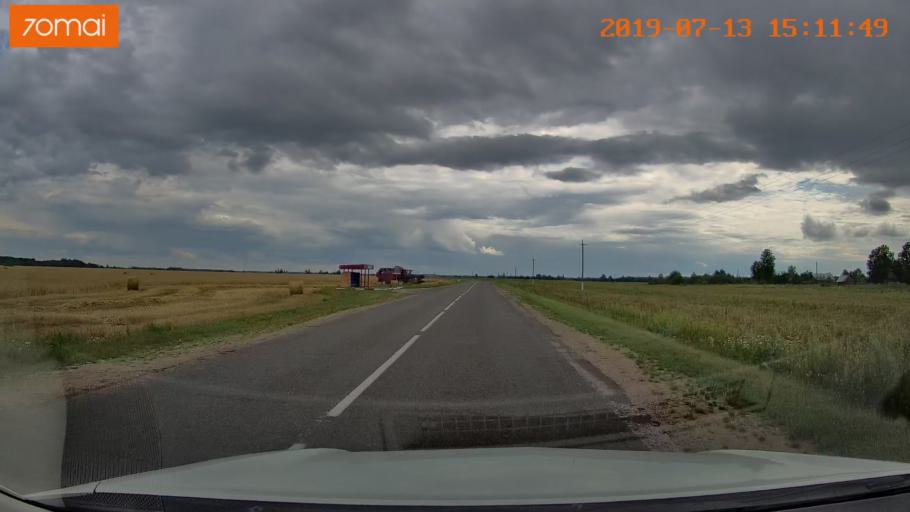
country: BY
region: Mogilev
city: Hlusha
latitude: 53.1562
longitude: 28.7869
